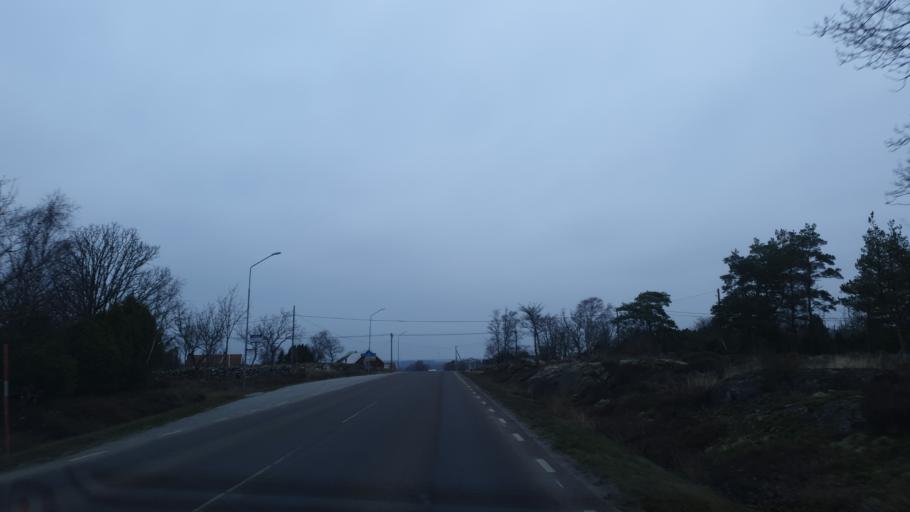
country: SE
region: Blekinge
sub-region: Karlskrona Kommun
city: Sturko
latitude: 56.1305
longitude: 15.7388
